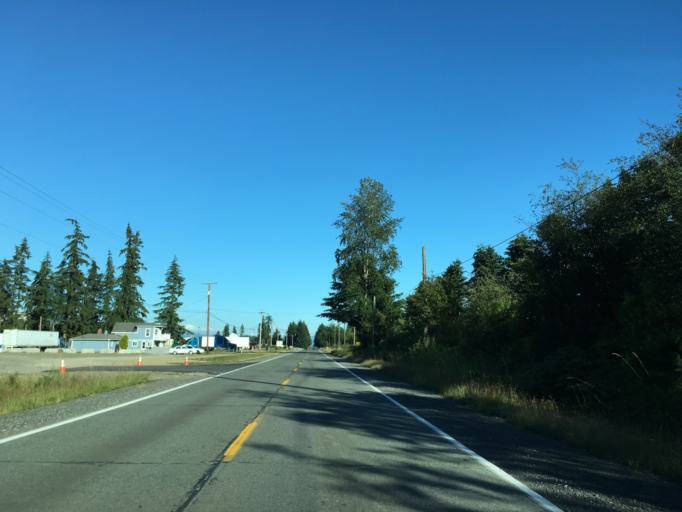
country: US
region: Washington
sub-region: Whatcom County
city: Birch Bay
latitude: 48.9431
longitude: -122.6792
